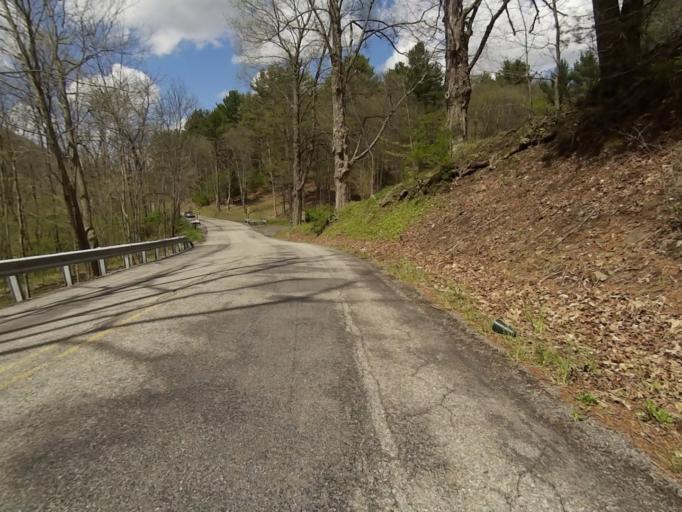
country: US
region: Pennsylvania
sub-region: Centre County
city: Milesburg
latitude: 40.9360
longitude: -77.8771
